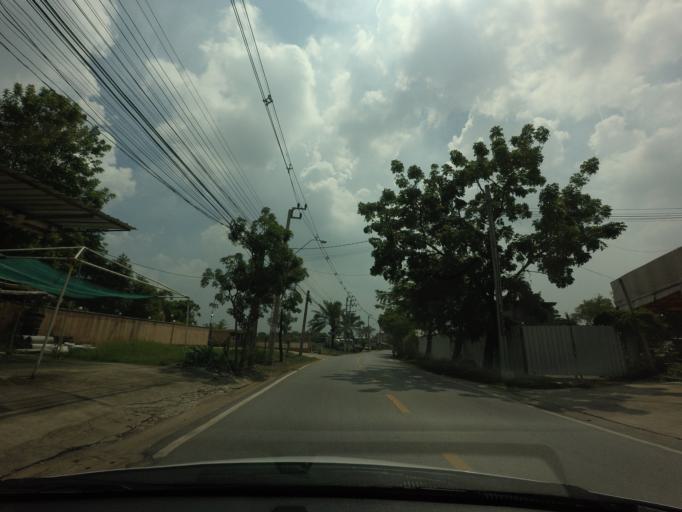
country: TH
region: Bangkok
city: Taling Chan
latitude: 13.7748
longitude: 100.4131
